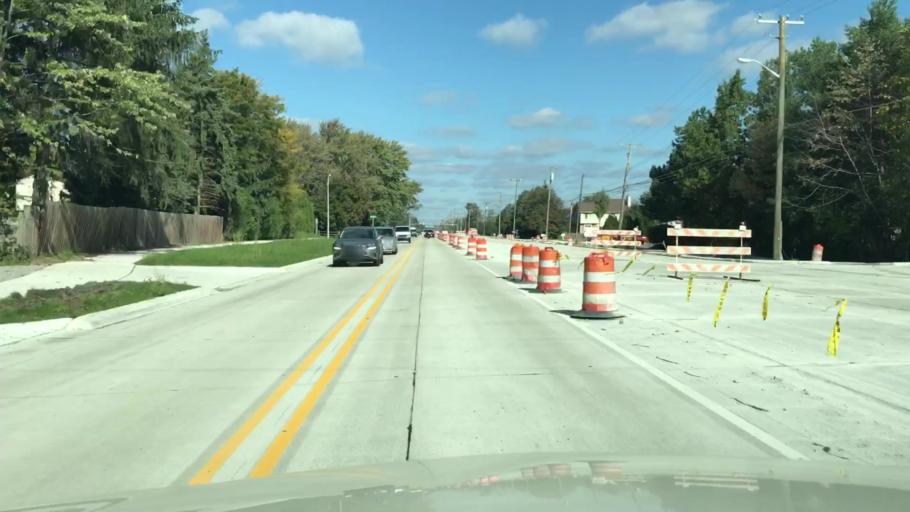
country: US
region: Michigan
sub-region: Oakland County
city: Troy
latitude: 42.6023
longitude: -83.0904
